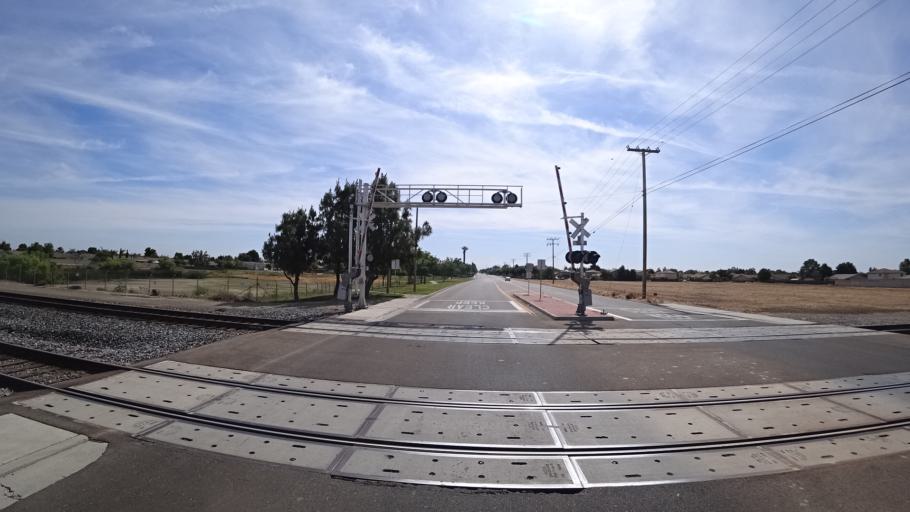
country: US
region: California
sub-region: Kings County
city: Lucerne
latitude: 36.3573
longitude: -119.6642
